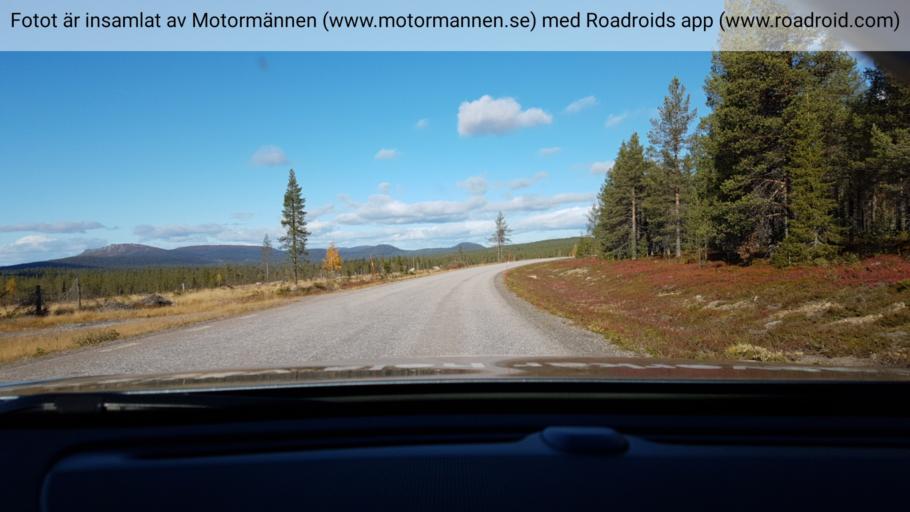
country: SE
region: Norrbotten
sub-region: Arjeplogs Kommun
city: Arjeplog
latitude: 65.8143
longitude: 18.4477
